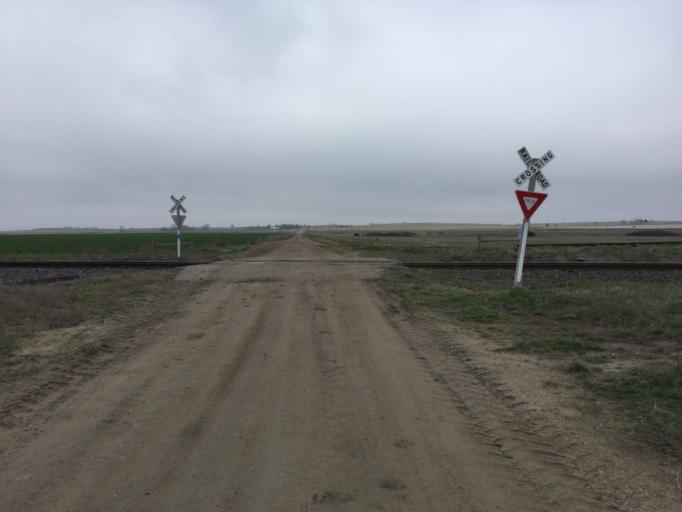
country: US
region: Kansas
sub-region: Russell County
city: Russell
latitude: 38.8364
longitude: -98.5394
